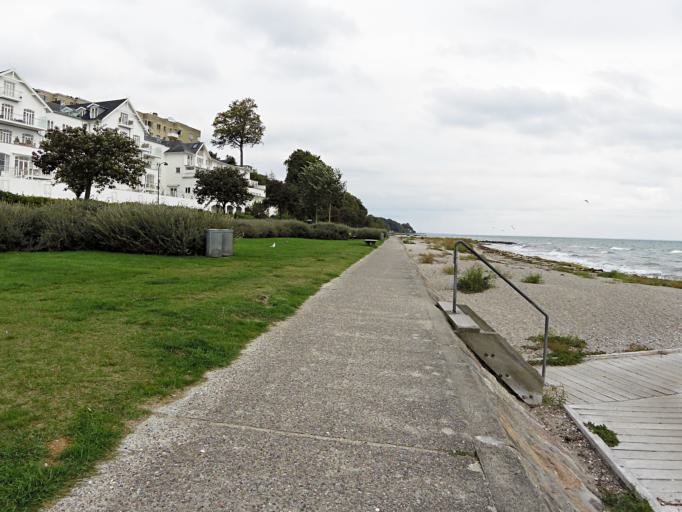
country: DK
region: Capital Region
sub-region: Rudersdal Kommune
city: Trorod
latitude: 55.8278
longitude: 12.5747
